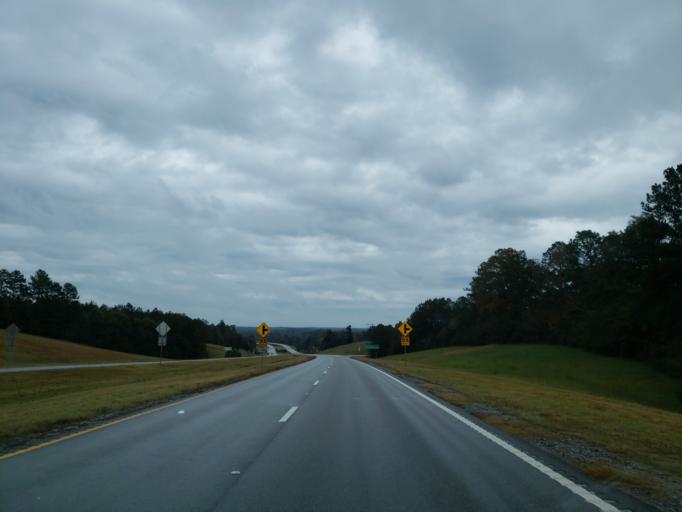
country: US
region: Mississippi
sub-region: Wayne County
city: Waynesboro
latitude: 31.6827
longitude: -88.6913
